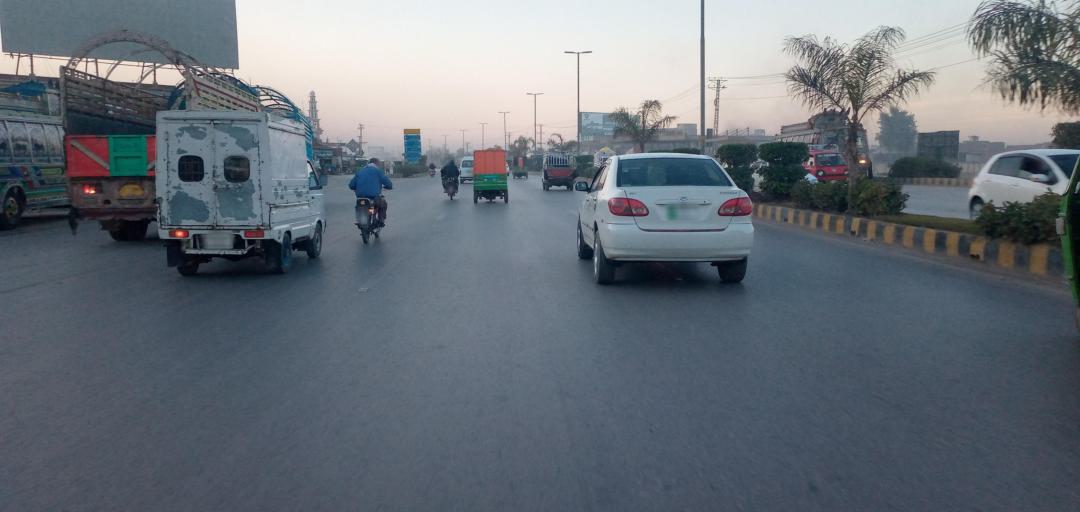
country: PK
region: Khyber Pakhtunkhwa
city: Peshawar
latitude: 34.0275
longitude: 71.6170
